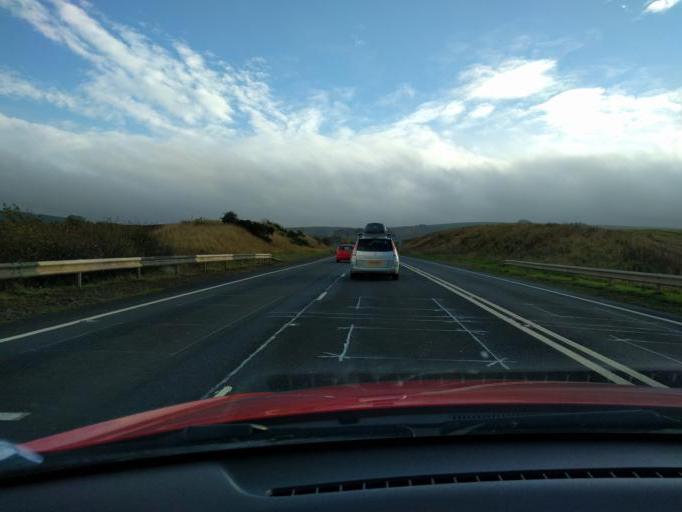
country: GB
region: Scotland
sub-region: The Scottish Borders
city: Duns
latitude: 55.9311
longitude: -2.3554
